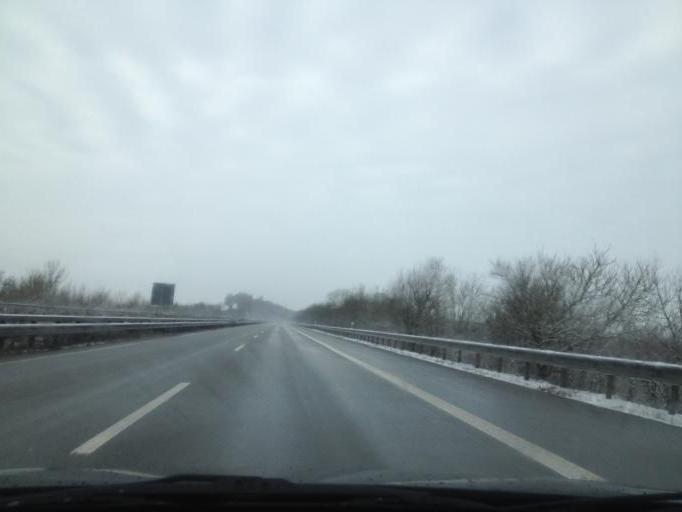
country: DE
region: Rheinland-Pfalz
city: Kleinsteinhausen
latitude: 49.2189
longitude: 7.4630
